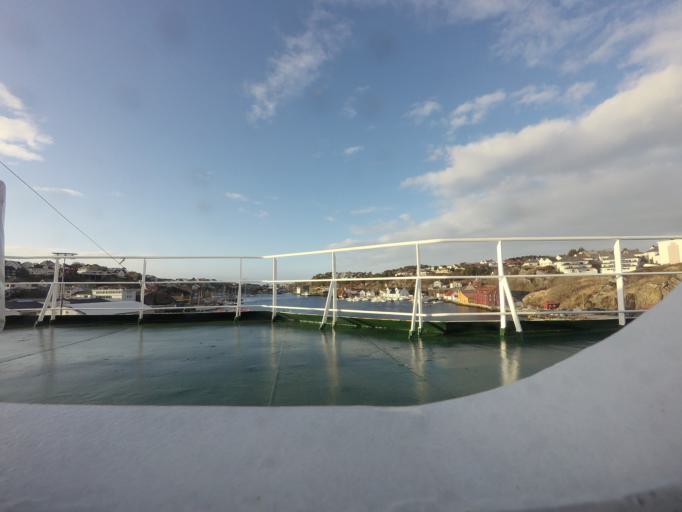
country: NO
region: More og Romsdal
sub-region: Kristiansund
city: Kristiansund
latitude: 63.1149
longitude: 7.7370
